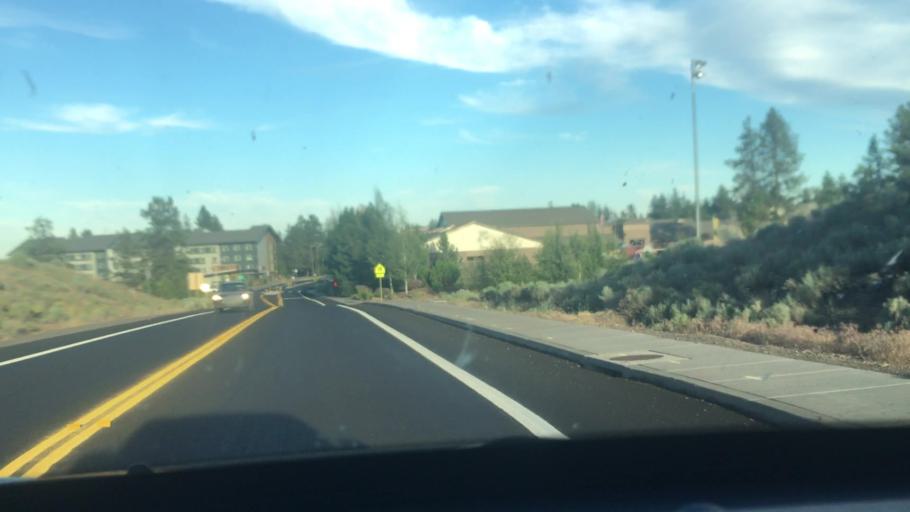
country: US
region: Oregon
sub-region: Deschutes County
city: Bend
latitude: 44.0402
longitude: -121.3397
